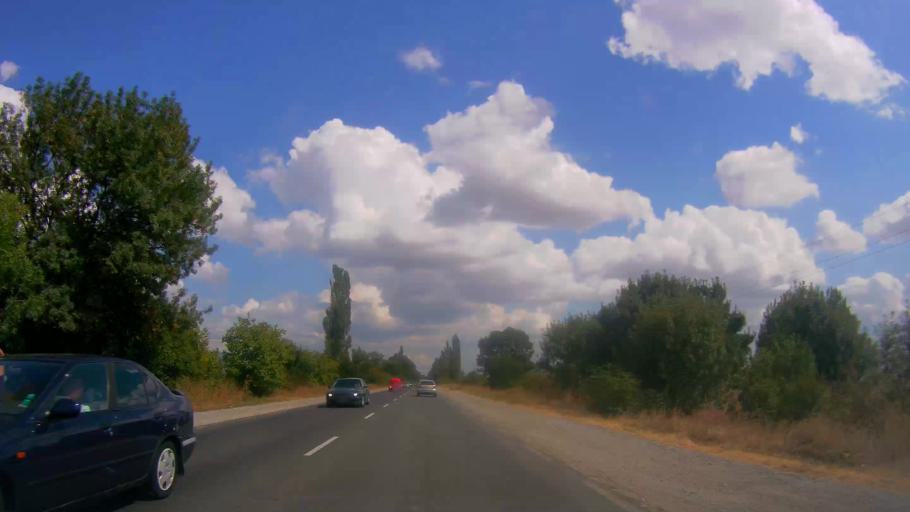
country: BG
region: Sliven
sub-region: Obshtina Sliven
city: Sliven
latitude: 42.6373
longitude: 26.2540
